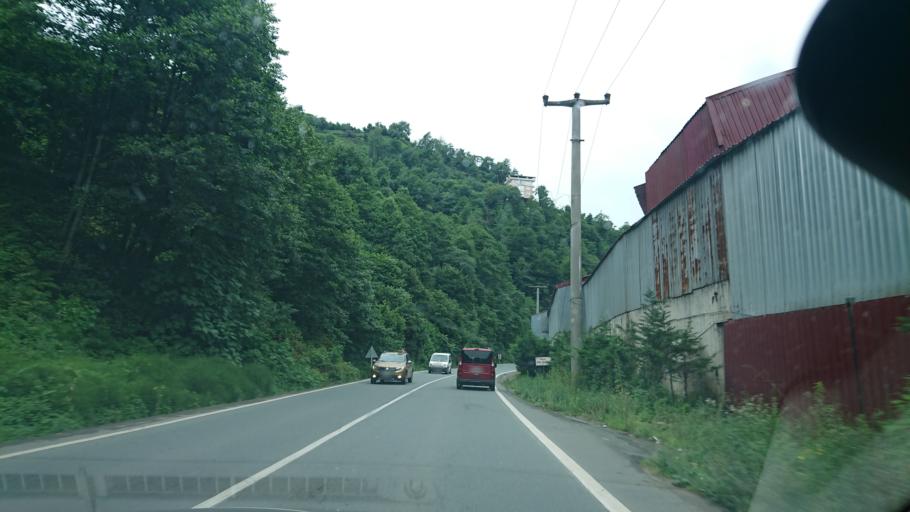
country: TR
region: Rize
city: Gundogdu
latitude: 41.0340
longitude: 40.5805
